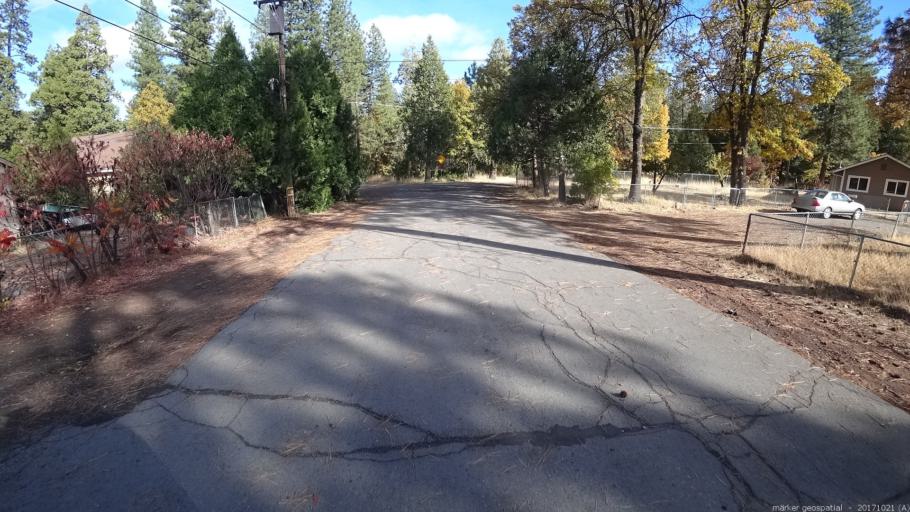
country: US
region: California
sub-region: Shasta County
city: Burney
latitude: 40.8782
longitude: -121.6716
